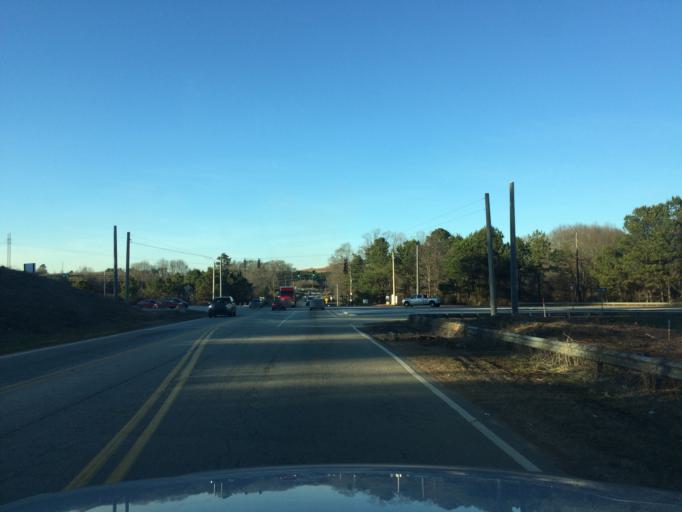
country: US
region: Georgia
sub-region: Barrow County
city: Winder
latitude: 33.9521
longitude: -83.7679
